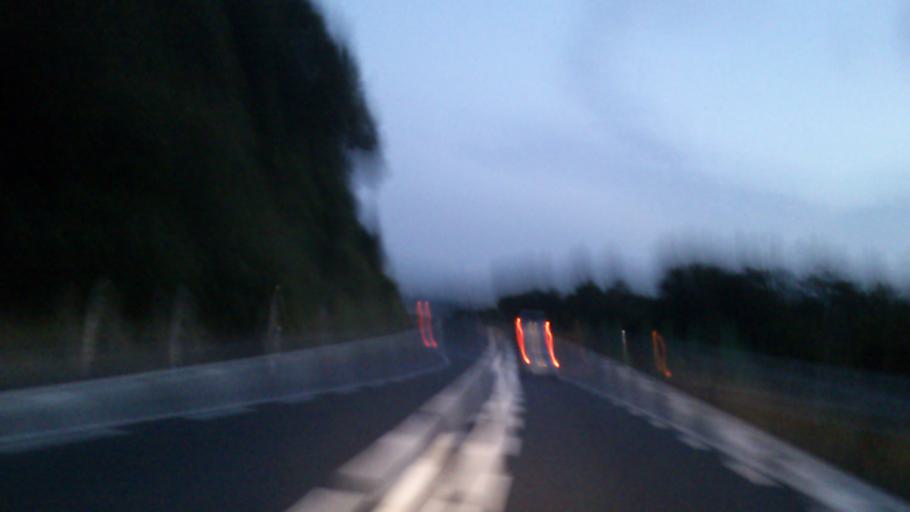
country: JP
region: Aichi
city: Kasugai
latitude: 35.3213
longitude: 137.0201
